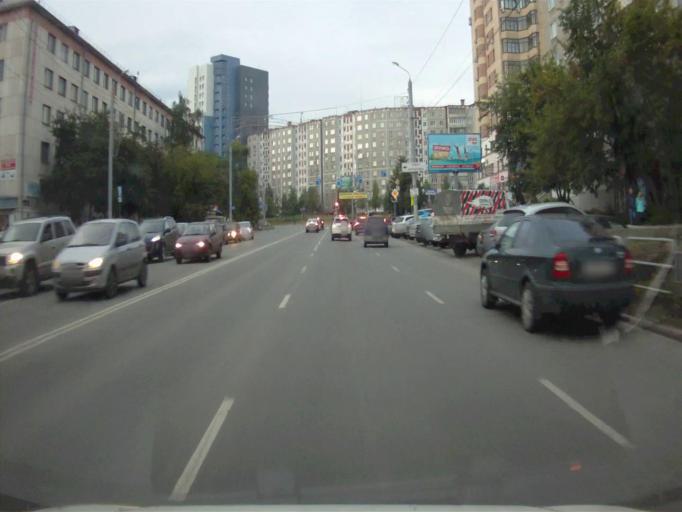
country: RU
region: Chelyabinsk
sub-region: Gorod Chelyabinsk
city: Chelyabinsk
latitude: 55.1544
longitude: 61.3815
